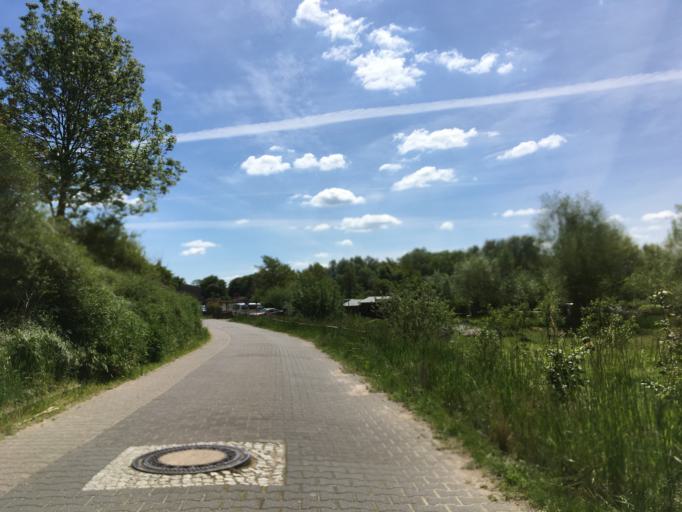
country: DE
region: Brandenburg
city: Niederfinow
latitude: 52.8416
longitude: 13.9002
